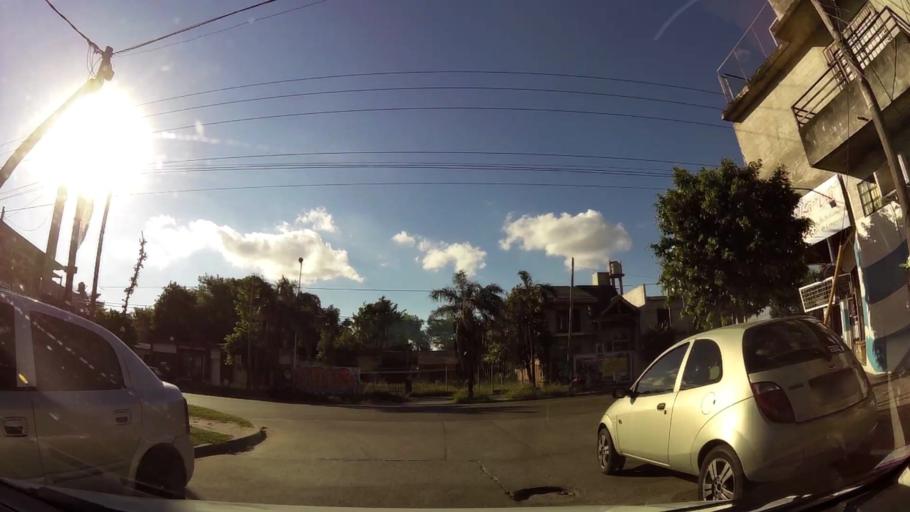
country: AR
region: Buenos Aires
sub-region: Partido de Moron
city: Moron
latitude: -34.6776
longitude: -58.6128
